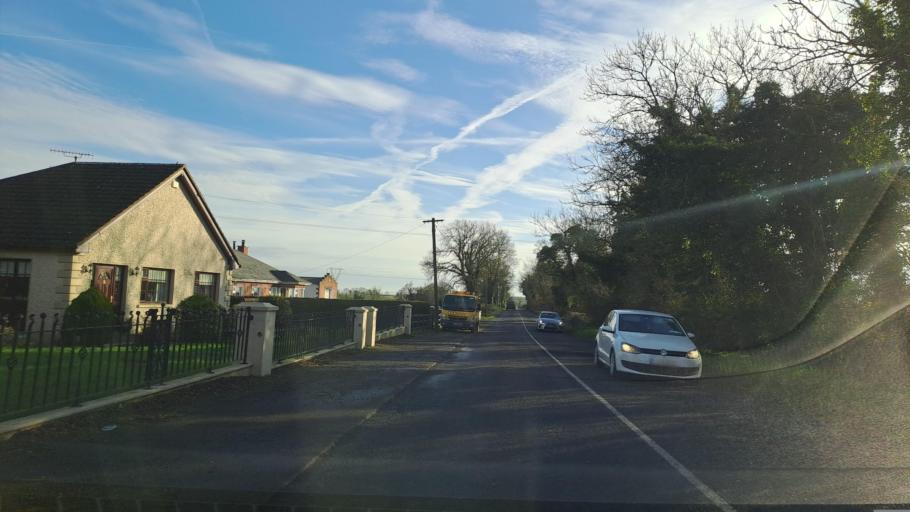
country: IE
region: Ulster
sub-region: An Cabhan
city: Kingscourt
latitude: 53.8785
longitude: -6.7232
